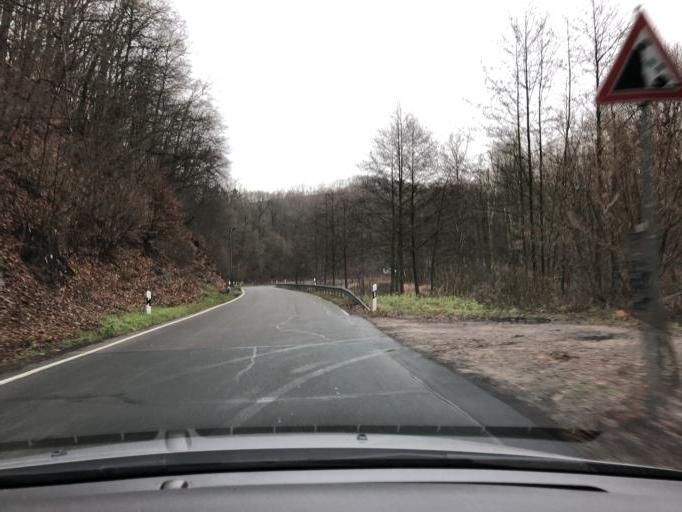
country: DE
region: Saxony
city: Rosswein
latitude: 51.0674
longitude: 13.1984
